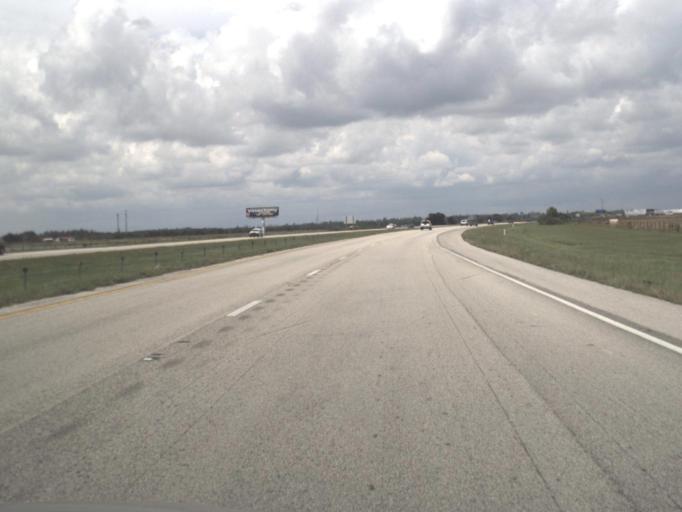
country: US
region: Florida
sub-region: Charlotte County
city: Charlotte Park
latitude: 26.8993
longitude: -82.0061
